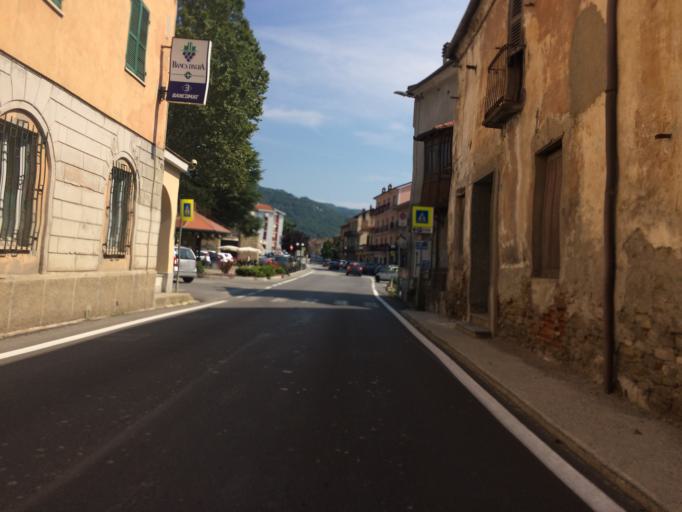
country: IT
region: Piedmont
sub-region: Provincia di Cuneo
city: Cortemilia
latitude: 44.5792
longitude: 8.1951
